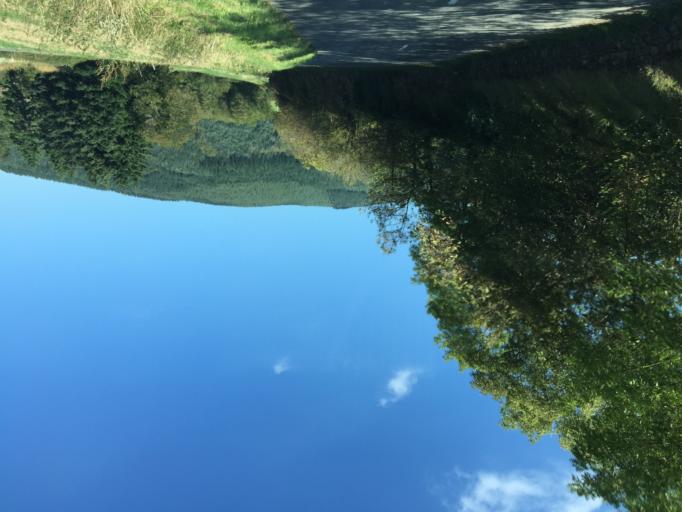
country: FR
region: Rhone-Alpes
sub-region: Departement de la Loire
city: Saint-Paul-en-Jarez
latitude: 45.4326
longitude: 4.5759
